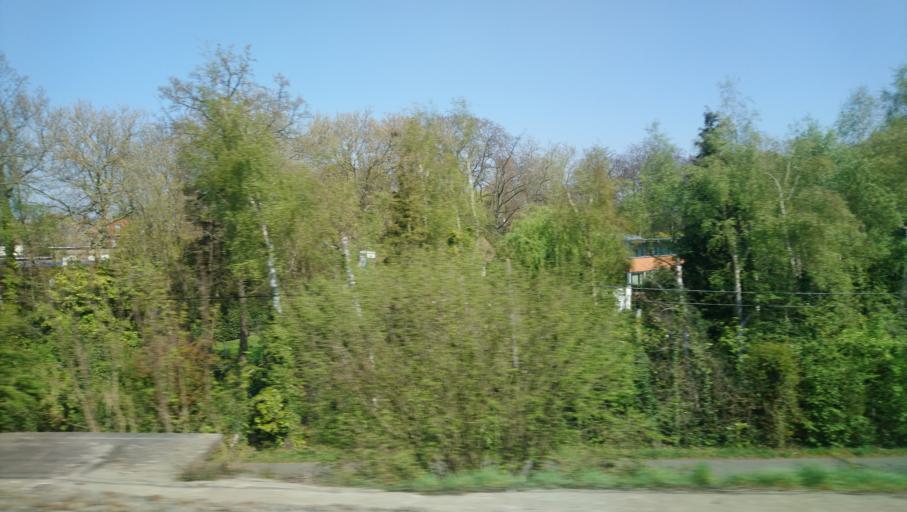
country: BE
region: Flanders
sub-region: Provincie Oost-Vlaanderen
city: Merelbeke
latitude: 51.0124
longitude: 3.7634
